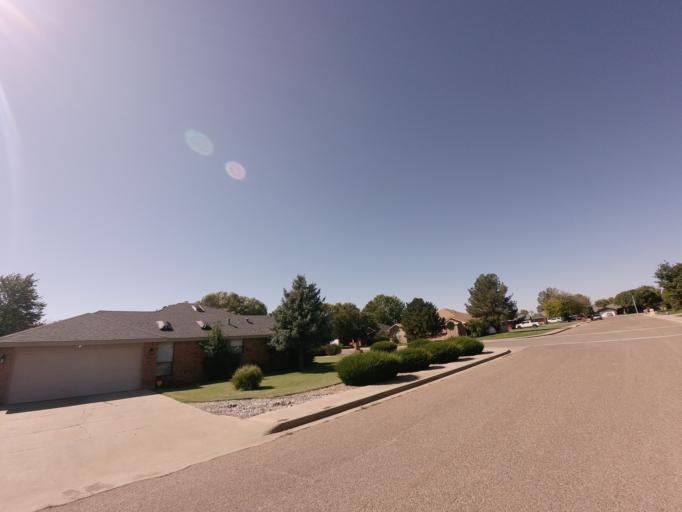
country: US
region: New Mexico
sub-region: Curry County
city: Clovis
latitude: 34.4307
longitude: -103.1742
